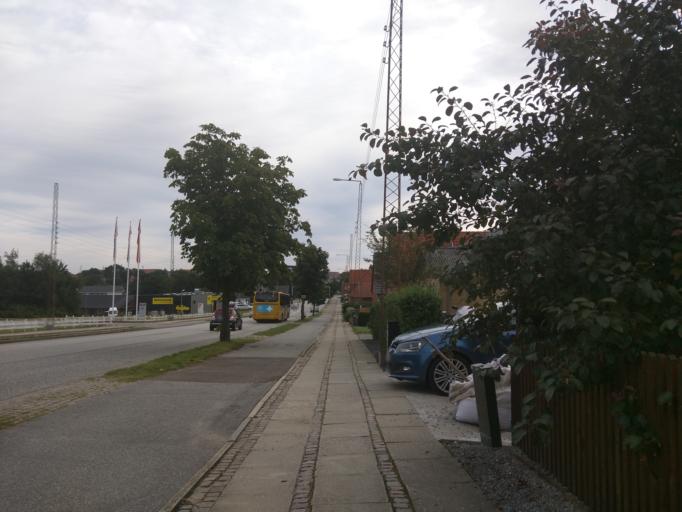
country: DK
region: Central Jutland
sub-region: Viborg Kommune
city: Viborg
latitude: 56.4487
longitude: 9.3804
